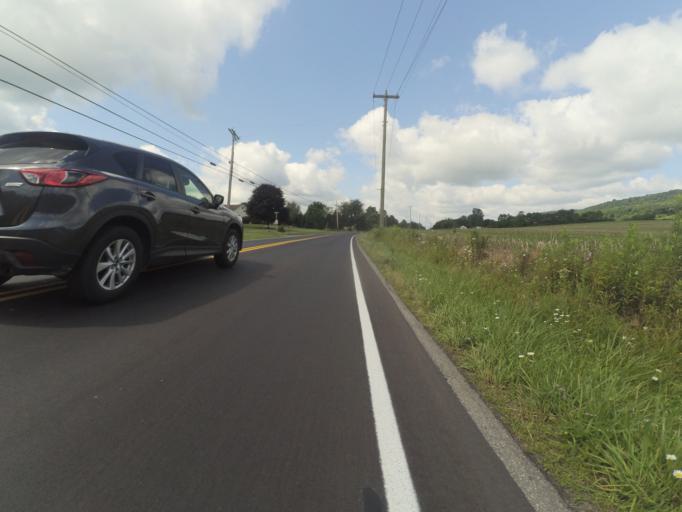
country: US
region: Pennsylvania
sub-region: Centre County
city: Stormstown
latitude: 40.8225
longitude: -77.9698
